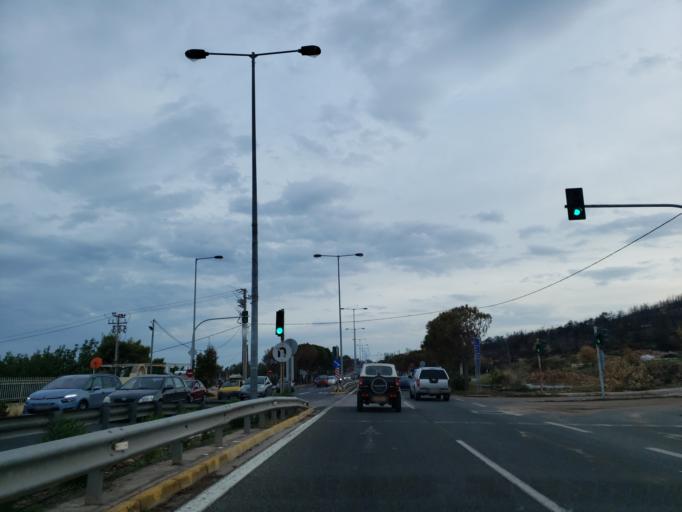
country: GR
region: Attica
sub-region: Nomarchia Anatolikis Attikis
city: Neos Voutzas
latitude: 38.0494
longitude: 23.9874
